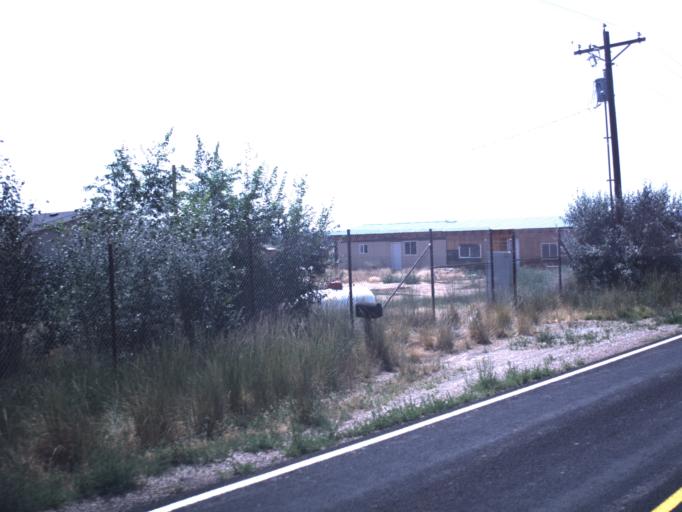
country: US
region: Utah
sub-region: Duchesne County
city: Roosevelt
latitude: 40.4037
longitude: -109.8236
